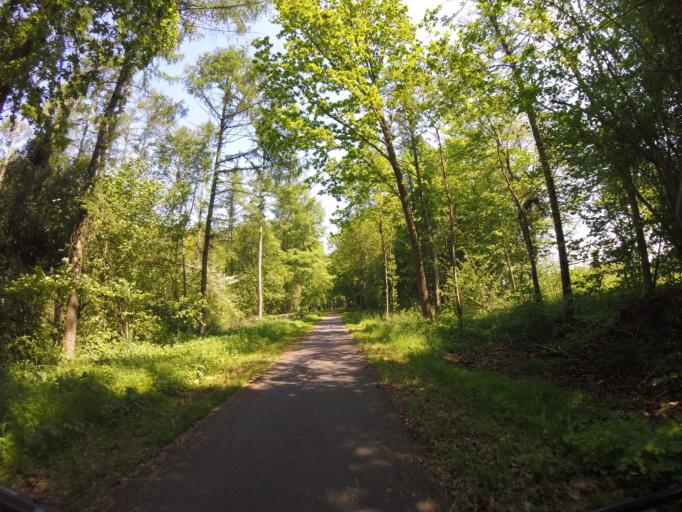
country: DE
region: Mecklenburg-Vorpommern
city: Bartenshagen-Parkentin
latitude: 54.1076
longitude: 11.9540
